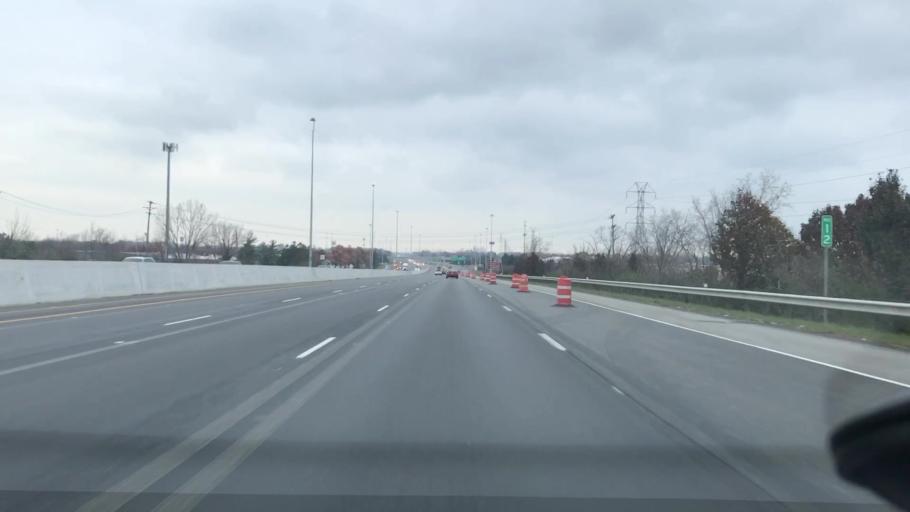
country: US
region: Ohio
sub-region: Franklin County
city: Hilliard
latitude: 40.0240
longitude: -83.1217
